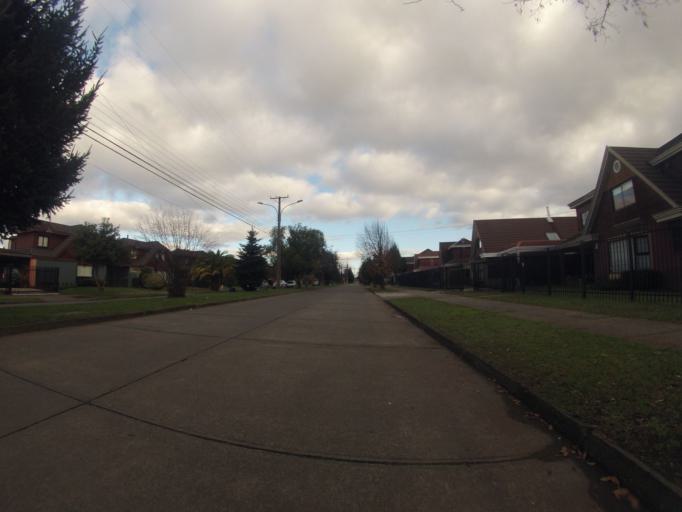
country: CL
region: Araucania
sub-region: Provincia de Cautin
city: Temuco
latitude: -38.7373
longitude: -72.6405
